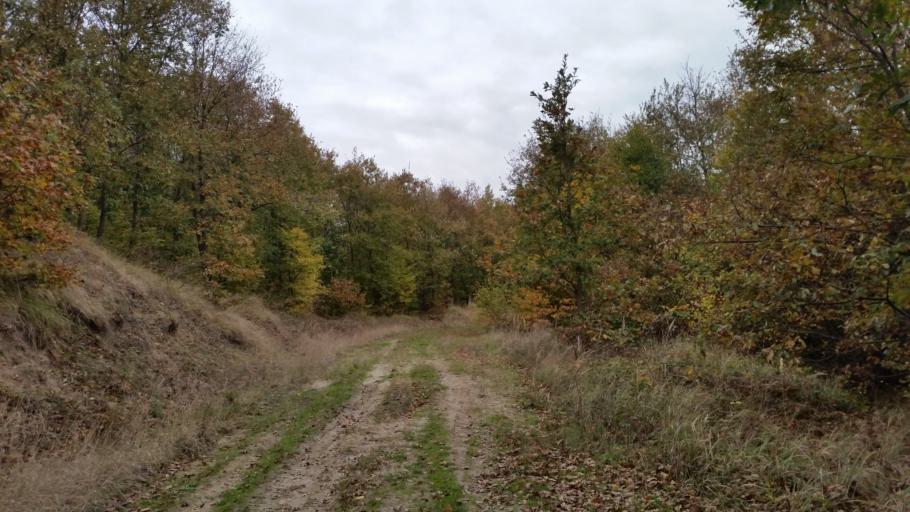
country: TR
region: Tekirdag
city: Cerkezkoey
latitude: 41.3787
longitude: 27.9999
